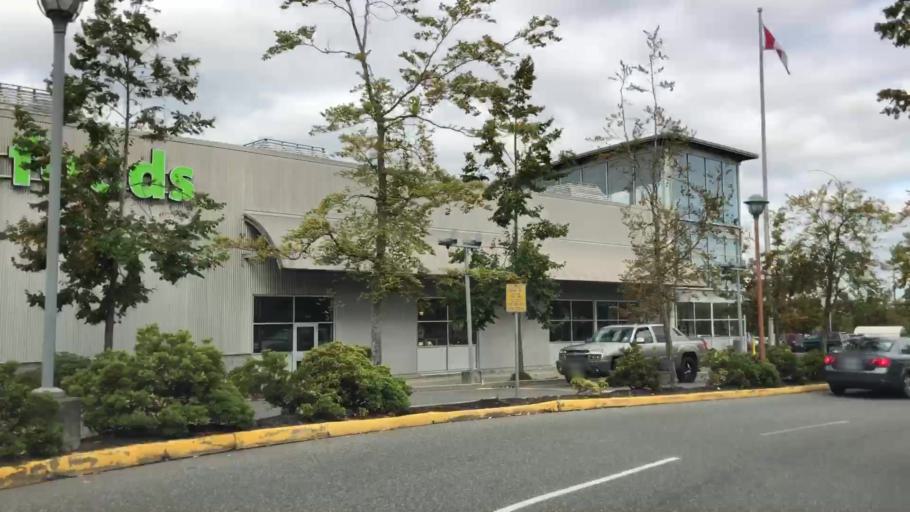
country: CA
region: British Columbia
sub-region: Greater Vancouver Regional District
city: White Rock
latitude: 49.0564
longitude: -122.8018
